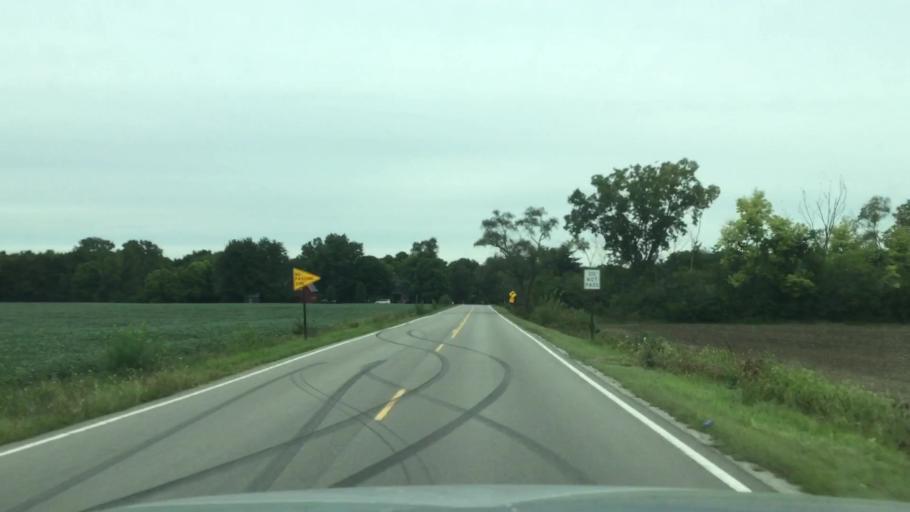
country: US
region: Michigan
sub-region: Washtenaw County
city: Milan
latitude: 42.0941
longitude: -83.7353
